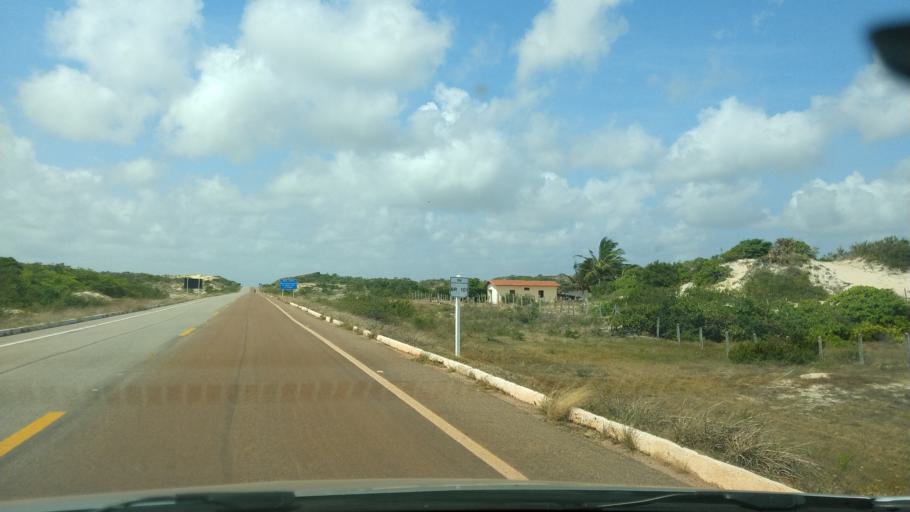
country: BR
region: Rio Grande do Norte
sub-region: Touros
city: Touros
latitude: -5.1586
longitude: -35.5005
